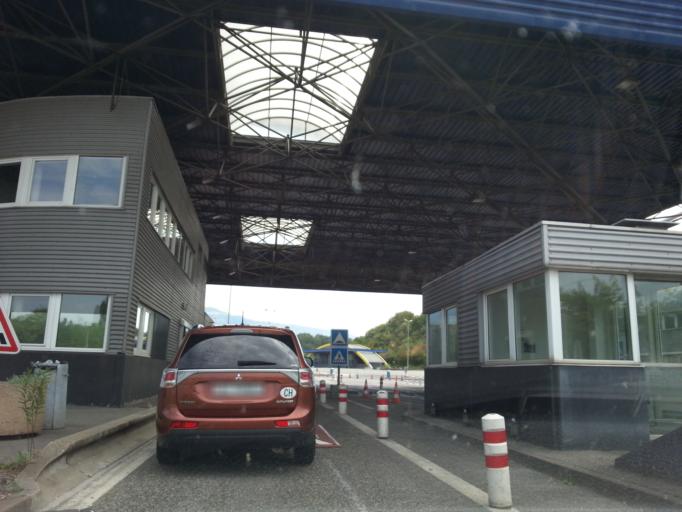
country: FR
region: Rhone-Alpes
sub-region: Departement de la Haute-Savoie
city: Saint-Julien-en-Genevois
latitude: 46.1469
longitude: 6.0954
